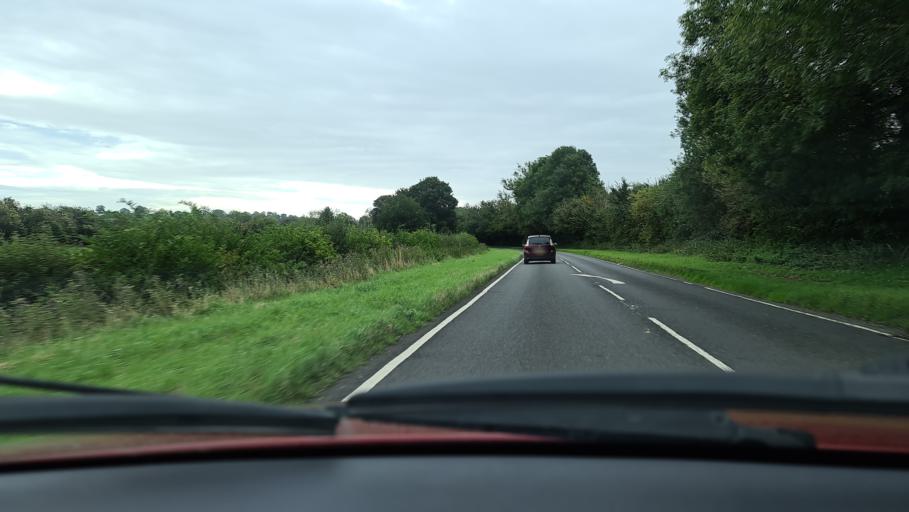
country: GB
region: England
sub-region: Buckinghamshire
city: Chesham
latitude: 51.7003
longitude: -0.6285
